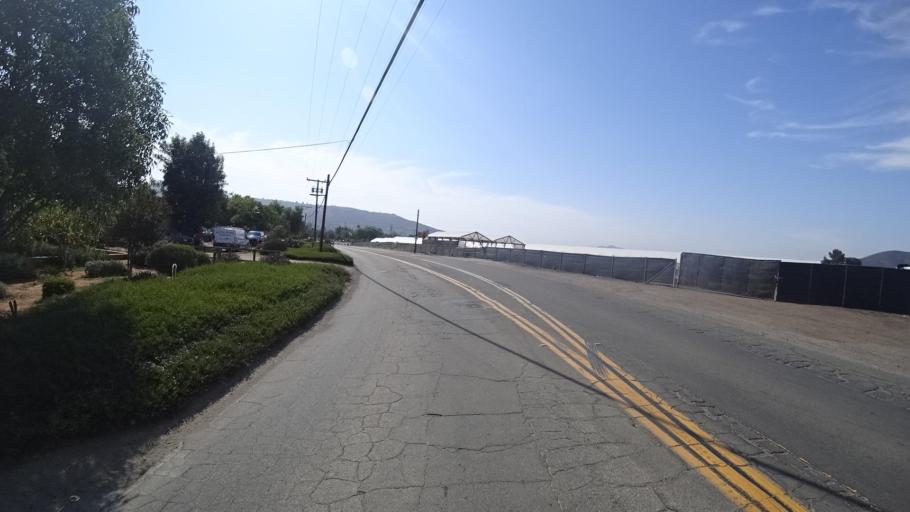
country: US
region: California
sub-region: San Diego County
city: San Marcos
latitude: 33.1867
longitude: -117.1564
